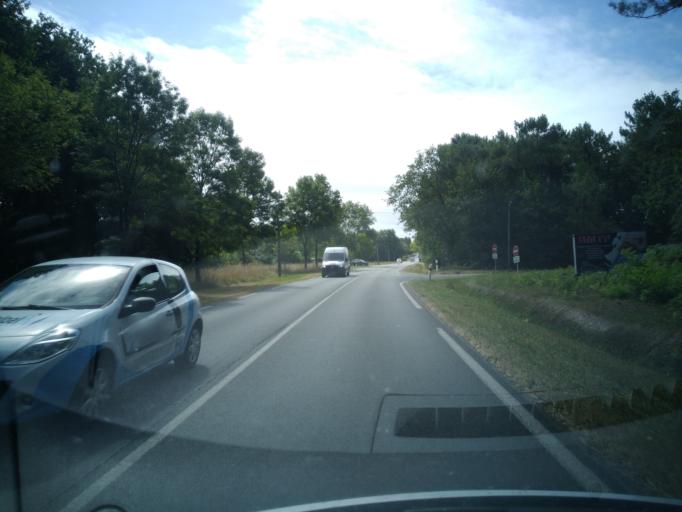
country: FR
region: Poitou-Charentes
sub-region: Departement de la Charente-Maritime
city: Chaillevette
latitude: 45.7154
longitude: -1.0684
